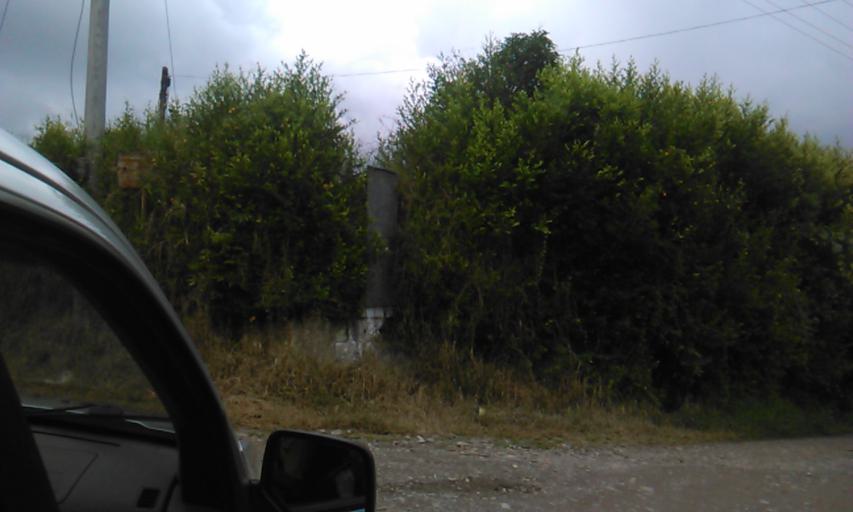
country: CO
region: Quindio
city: La Tebaida
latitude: 4.5127
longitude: -75.8541
